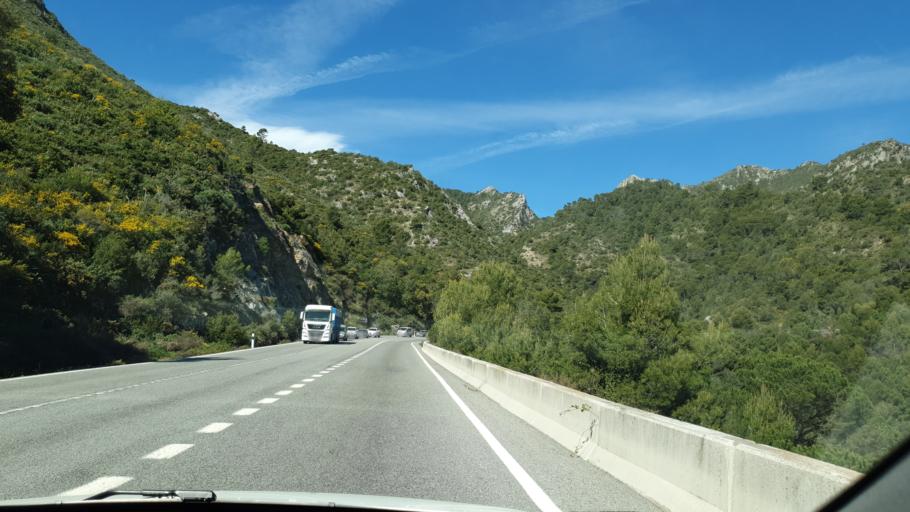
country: ES
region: Andalusia
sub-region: Provincia de Malaga
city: Ojen
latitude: 36.5662
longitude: -4.8630
